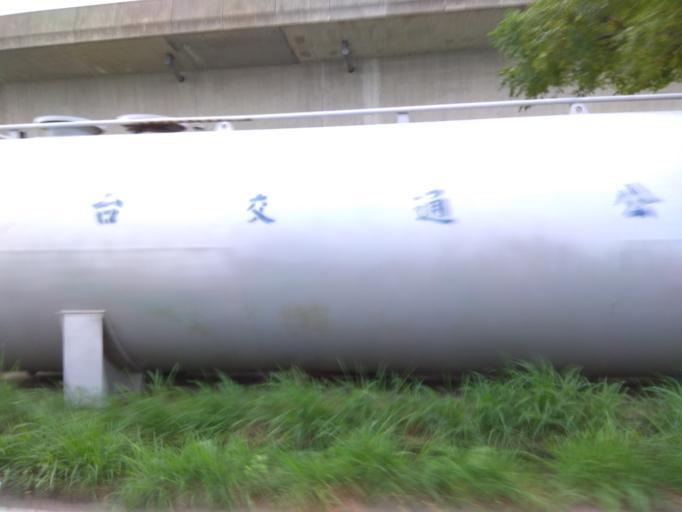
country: TW
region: Taiwan
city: Taoyuan City
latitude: 25.0462
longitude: 121.2146
